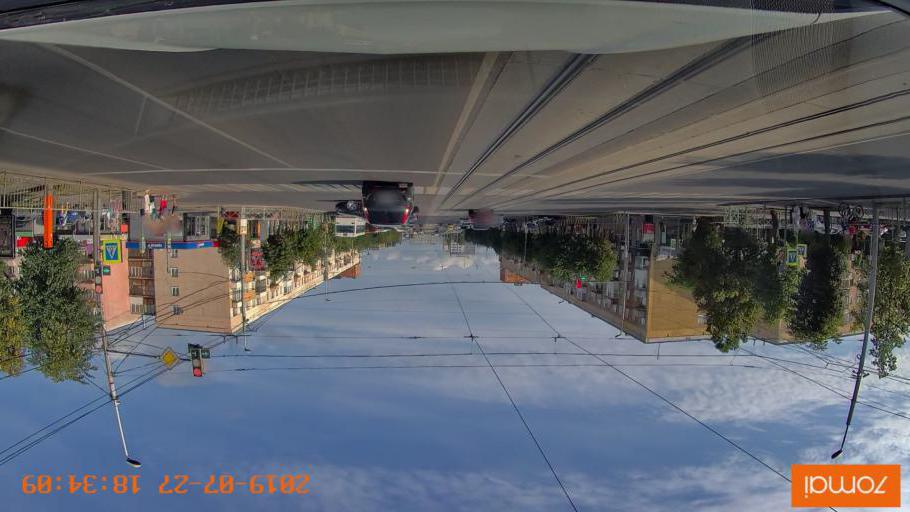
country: RU
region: Kaliningrad
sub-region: Gorod Kaliningrad
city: Kaliningrad
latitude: 54.7021
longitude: 20.5047
